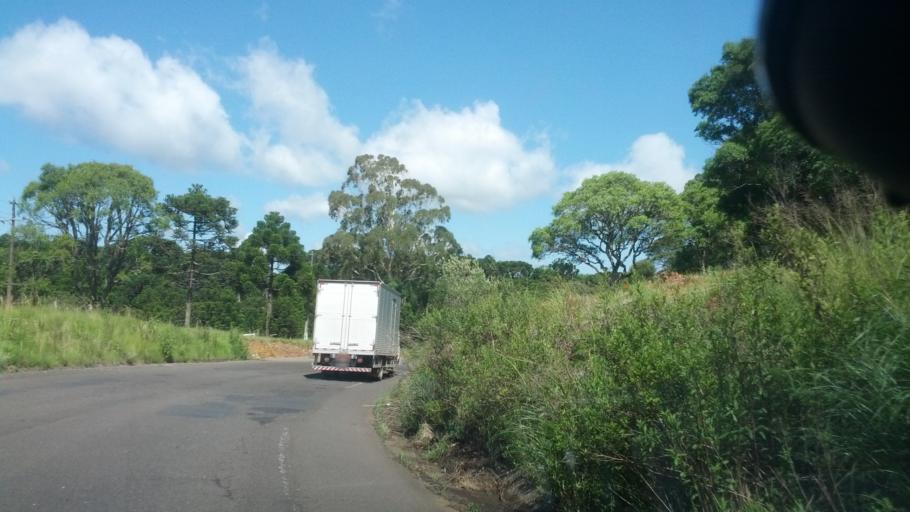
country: BR
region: Santa Catarina
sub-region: Lages
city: Lages
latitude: -27.9276
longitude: -50.5515
